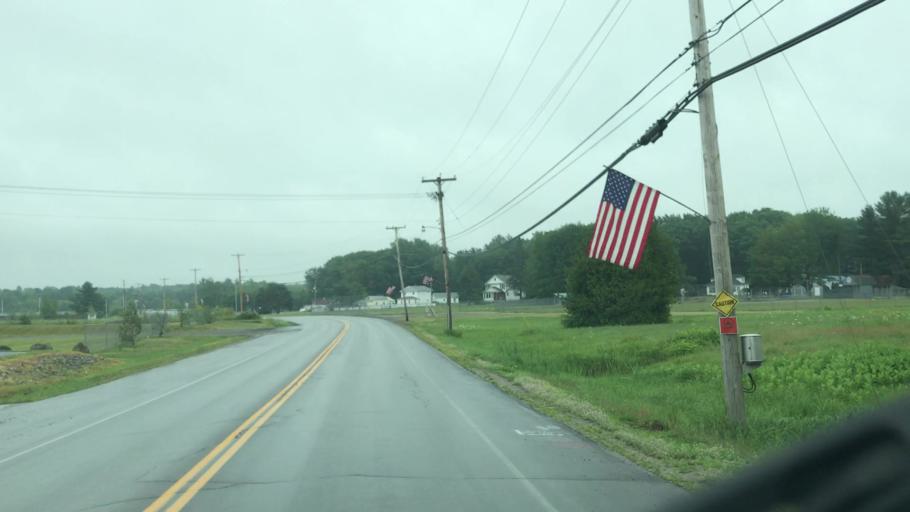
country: US
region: Maine
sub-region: Penobscot County
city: Howland
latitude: 45.2370
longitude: -68.6590
